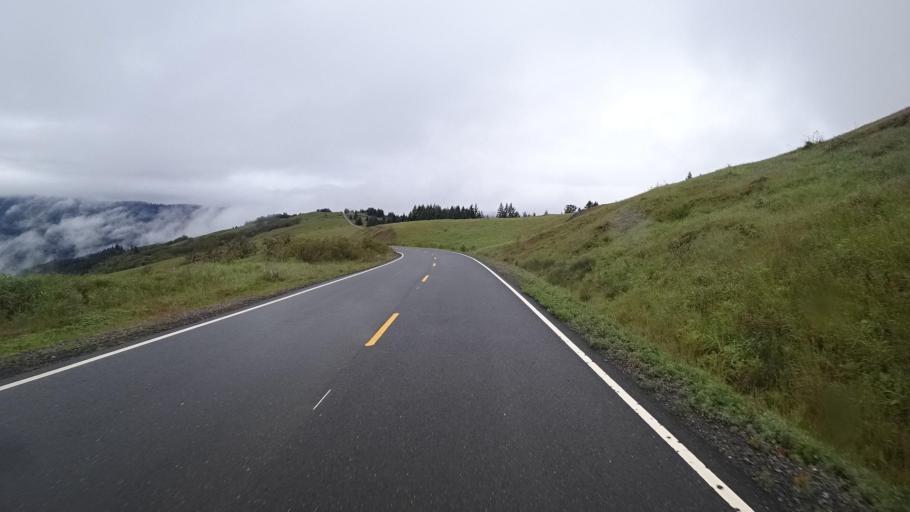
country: US
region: California
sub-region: Humboldt County
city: Westhaven-Moonstone
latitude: 41.1616
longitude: -123.8983
